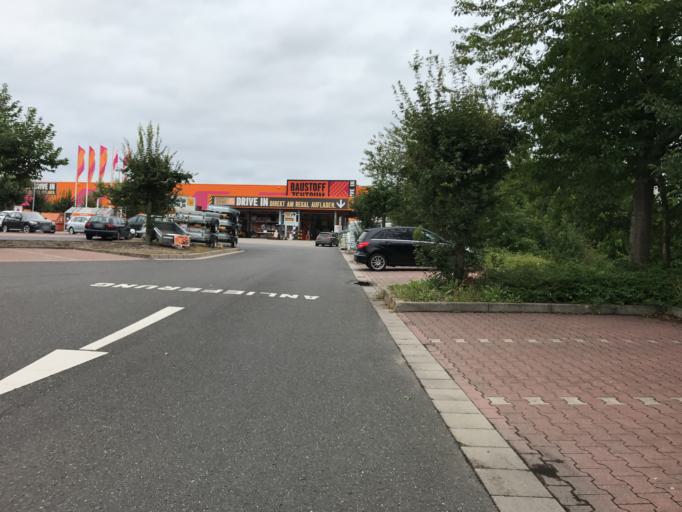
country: DE
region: Rheinland-Pfalz
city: Klein-Winternheim
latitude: 49.9661
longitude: 8.2382
